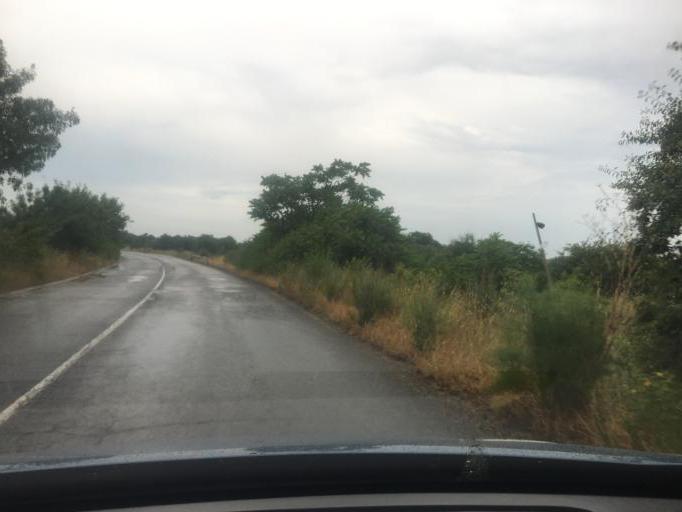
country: BG
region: Burgas
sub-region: Obshtina Burgas
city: Burgas
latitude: 42.5569
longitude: 27.4907
